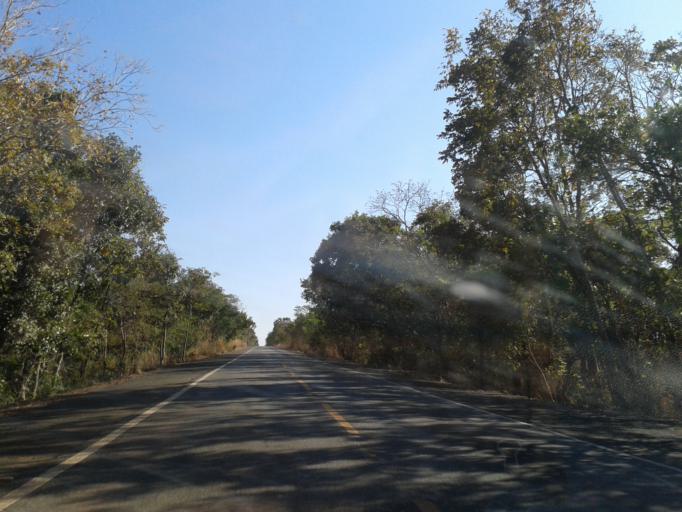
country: BR
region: Goias
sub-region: Mozarlandia
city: Mozarlandia
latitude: -14.8177
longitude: -50.5313
